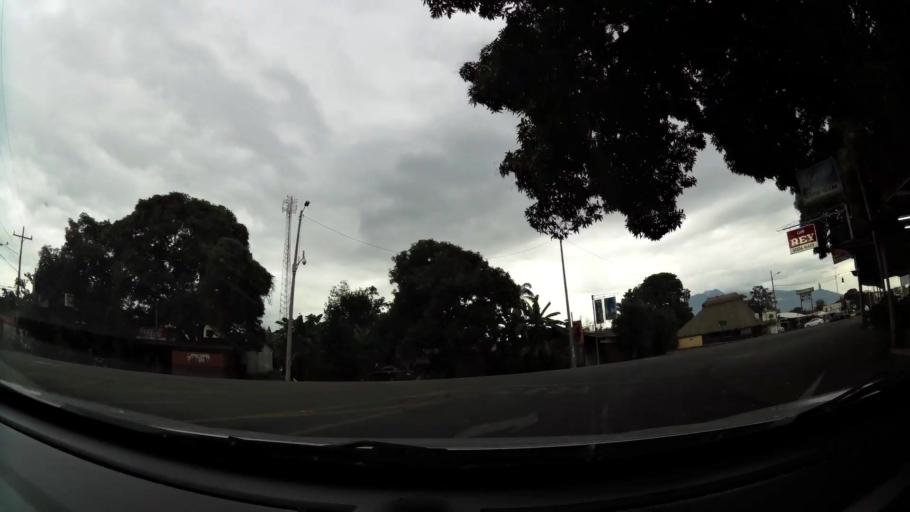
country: CR
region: Alajuela
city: Orotina
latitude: 9.9127
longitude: -84.5195
